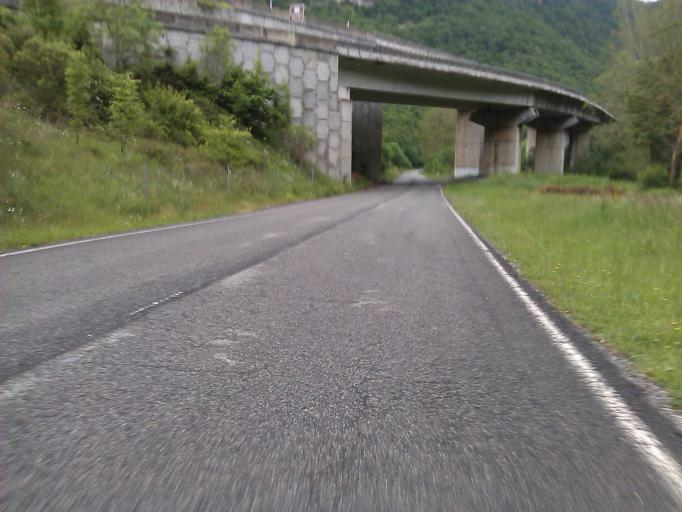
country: ES
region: Navarre
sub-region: Provincia de Navarra
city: Irurtzun
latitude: 42.9442
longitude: -1.8284
